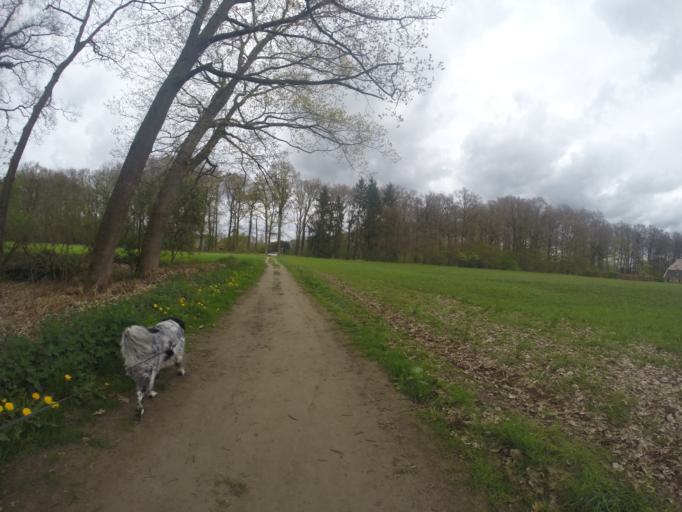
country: NL
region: Gelderland
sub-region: Gemeente Zutphen
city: Leesten
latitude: 52.1024
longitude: 6.2742
